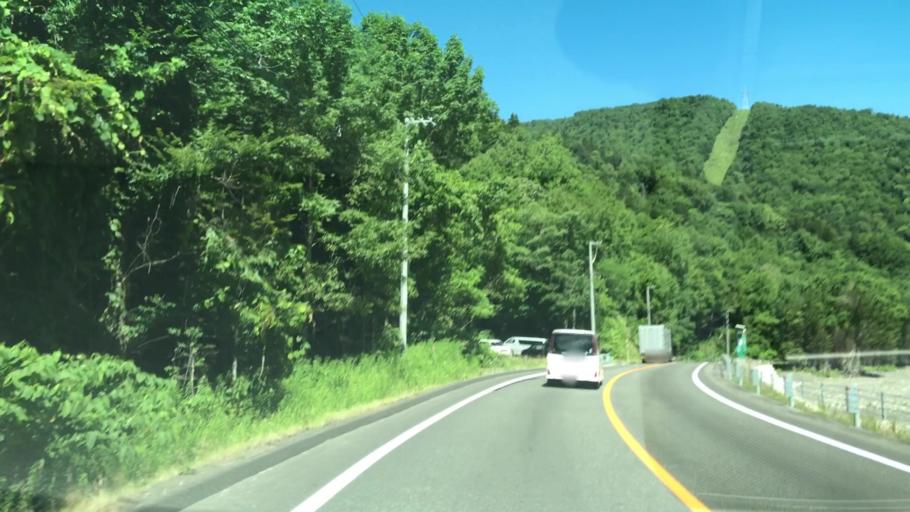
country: JP
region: Hokkaido
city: Shimo-furano
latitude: 42.9291
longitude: 142.5934
